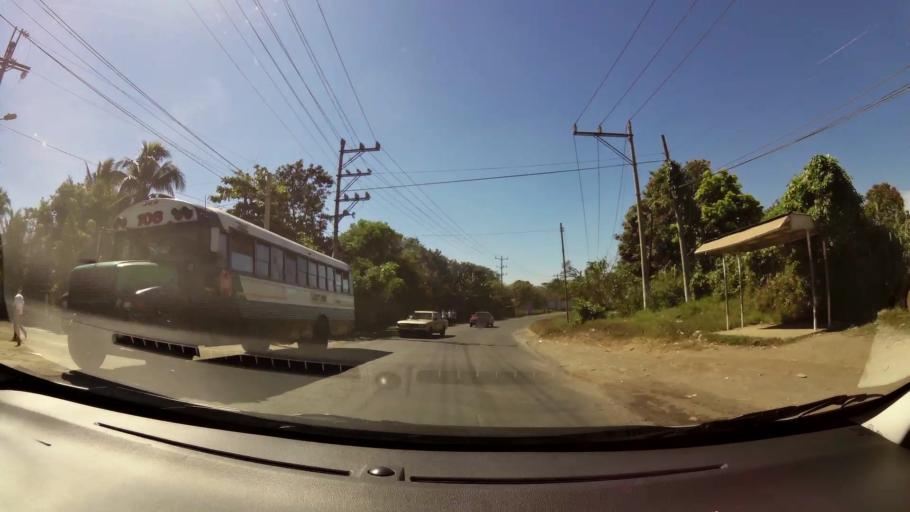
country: SV
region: La Libertad
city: San Juan Opico
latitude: 13.8032
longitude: -89.3593
